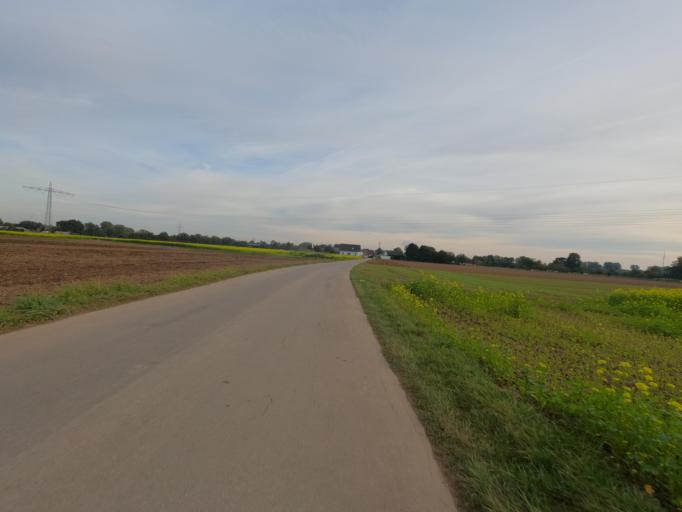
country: DE
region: North Rhine-Westphalia
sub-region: Regierungsbezirk Koln
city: Wassenberg
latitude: 51.0528
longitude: 6.1671
